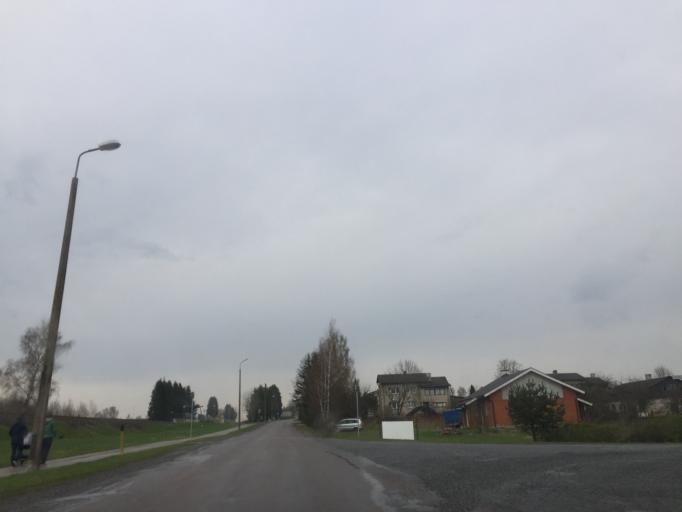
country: EE
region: Tartu
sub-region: UElenurme vald
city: Ulenurme
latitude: 58.3083
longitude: 26.7223
